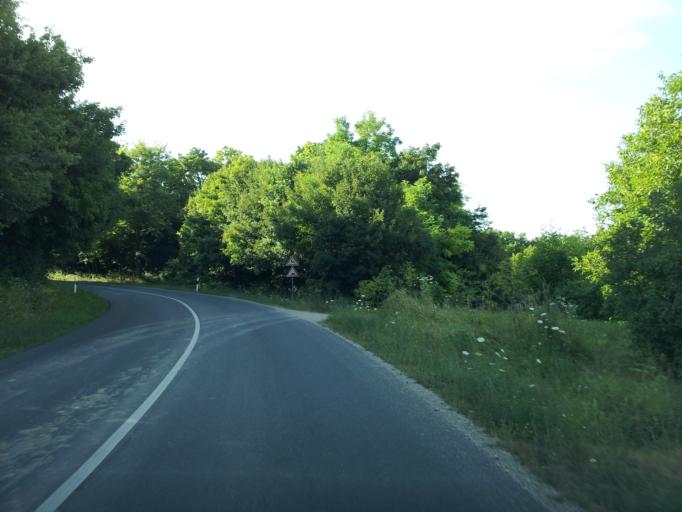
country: HU
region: Veszprem
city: Urkut
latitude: 47.0001
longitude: 17.6481
